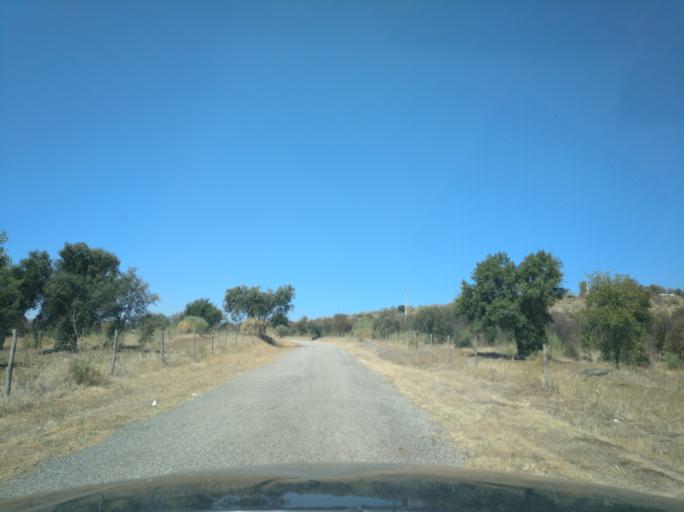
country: PT
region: Portalegre
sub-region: Campo Maior
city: Campo Maior
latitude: 39.0014
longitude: -7.0894
